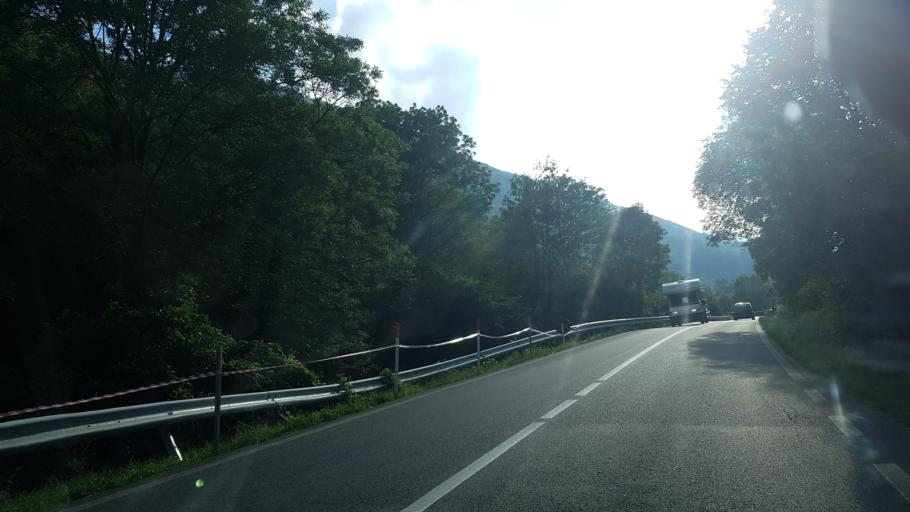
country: IT
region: Piedmont
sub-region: Provincia di Cuneo
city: Frassino
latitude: 44.5734
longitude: 7.2348
